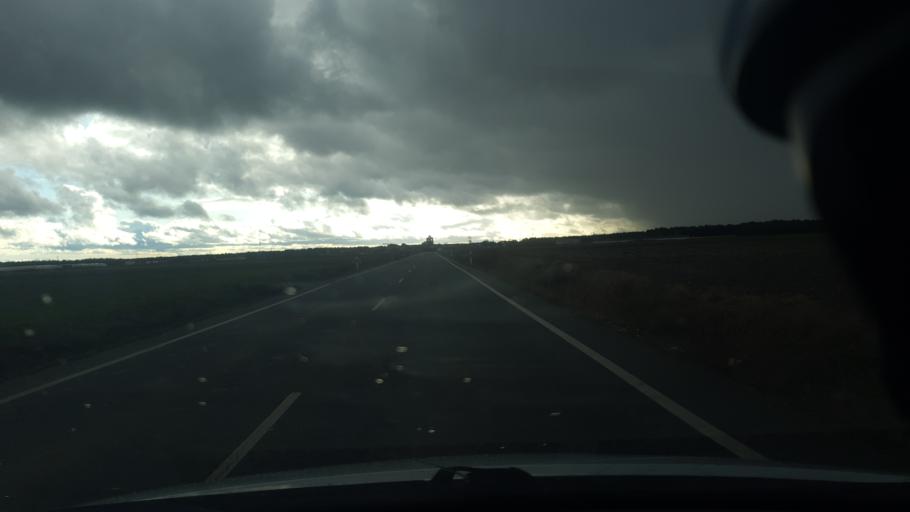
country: ES
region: Castille and Leon
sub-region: Provincia de Segovia
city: Chane
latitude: 41.3065
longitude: -4.3993
